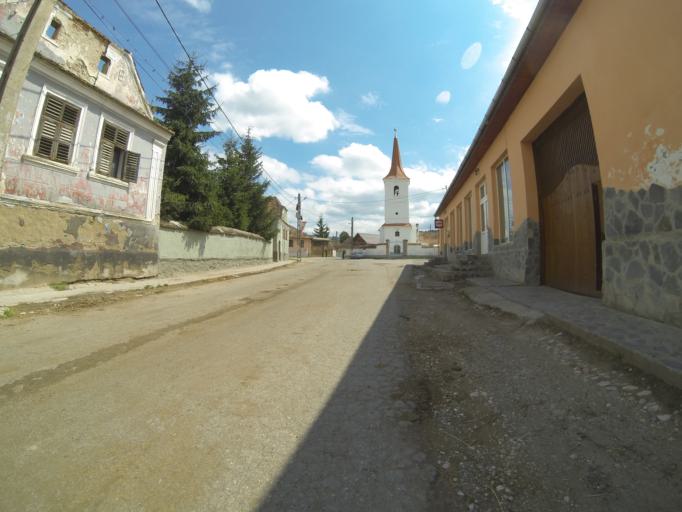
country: RO
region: Brasov
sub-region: Comuna Hoghiz
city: Hoghiz
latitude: 45.9826
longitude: 25.3826
